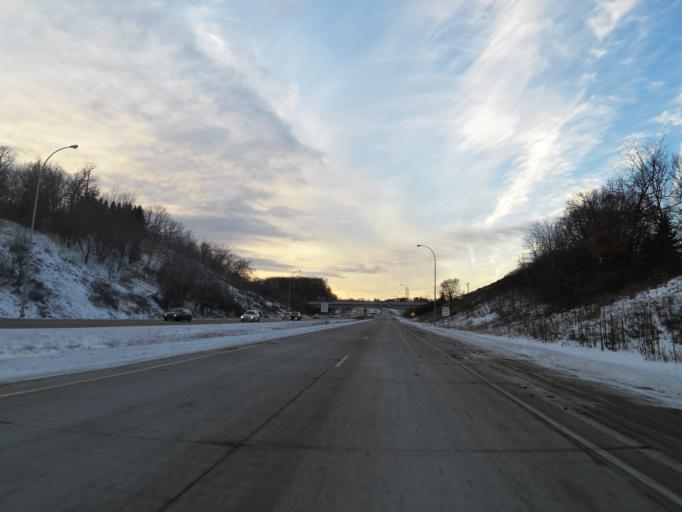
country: US
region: Minnesota
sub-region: Hennepin County
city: Hopkins
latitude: 44.8922
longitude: -93.4297
